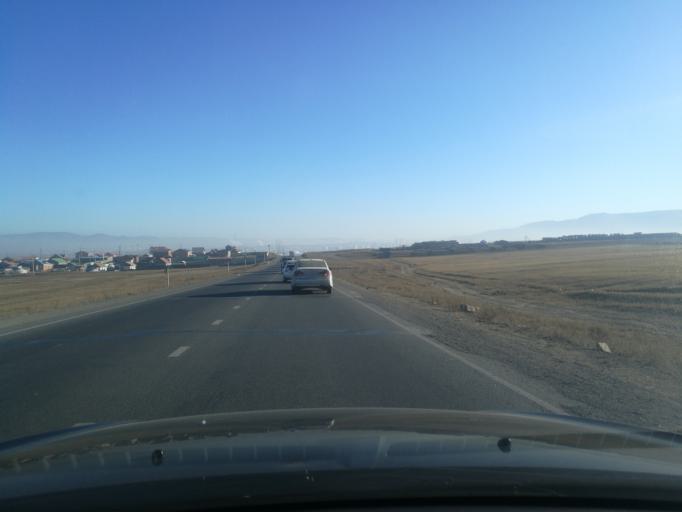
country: MN
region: Ulaanbaatar
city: Ulaanbaatar
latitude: 47.8412
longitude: 106.7233
